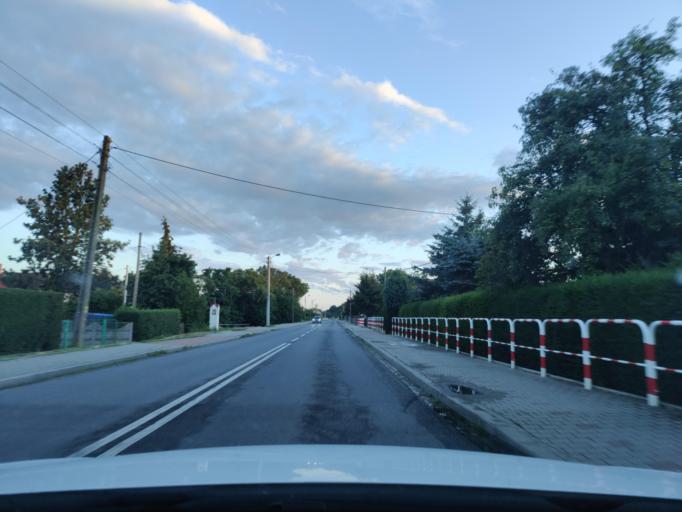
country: PL
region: Opole Voivodeship
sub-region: Powiat nyski
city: Chroscina
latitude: 50.6521
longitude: 17.3860
